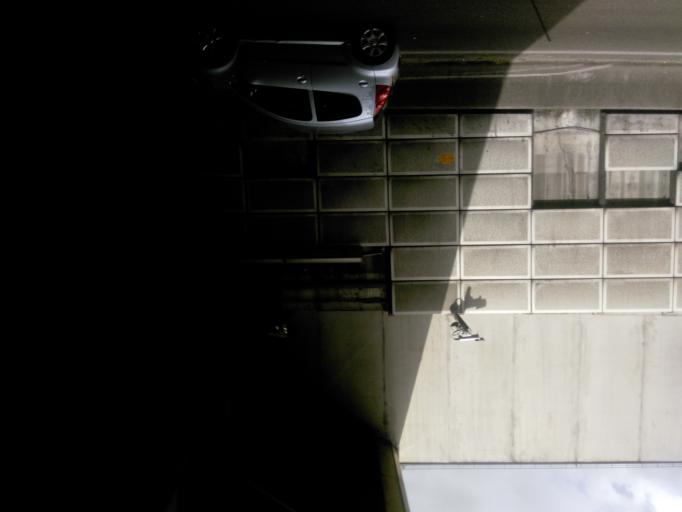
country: FR
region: Ile-de-France
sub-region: Departement de Seine-Saint-Denis
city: Saint-Denis
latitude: 48.9184
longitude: 2.3574
